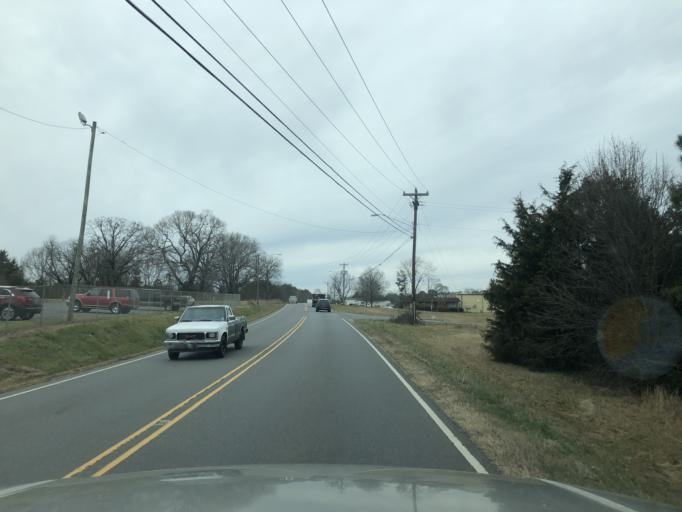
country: US
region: North Carolina
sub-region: Cleveland County
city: Shelby
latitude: 35.3001
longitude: -81.4856
